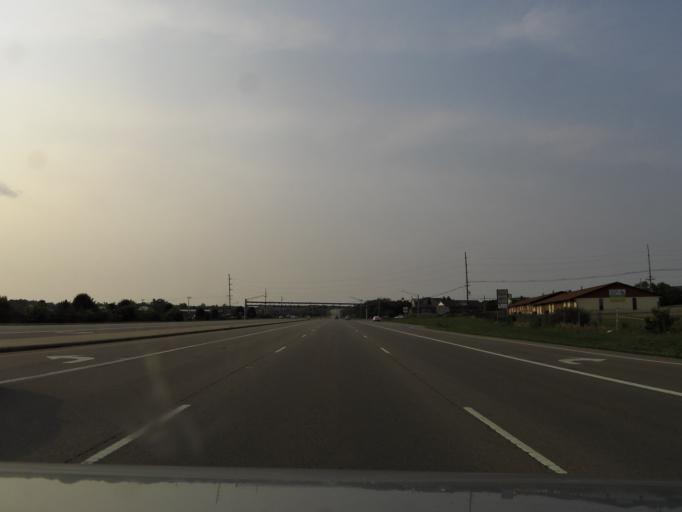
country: US
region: Ohio
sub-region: Butler County
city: Fairfield
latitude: 39.3607
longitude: -84.5036
